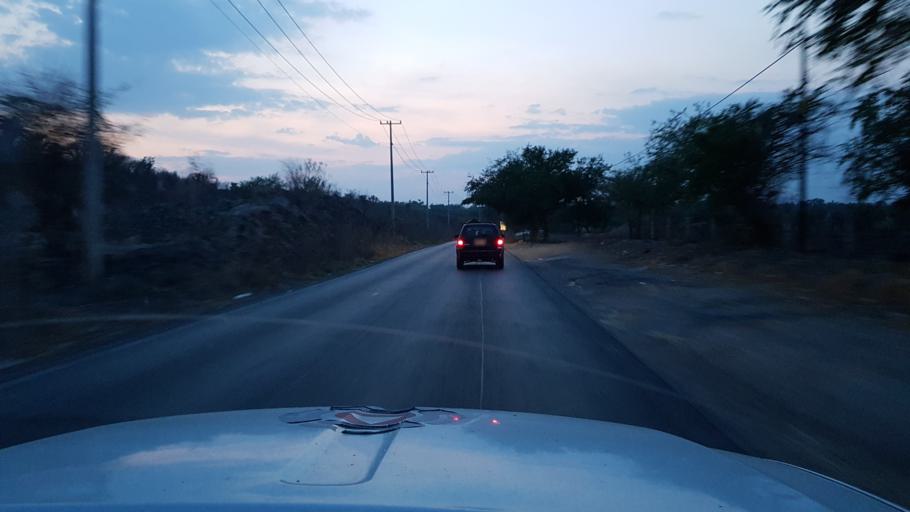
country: MX
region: Morelos
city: Tlaltizapan
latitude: 18.6891
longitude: -99.1414
